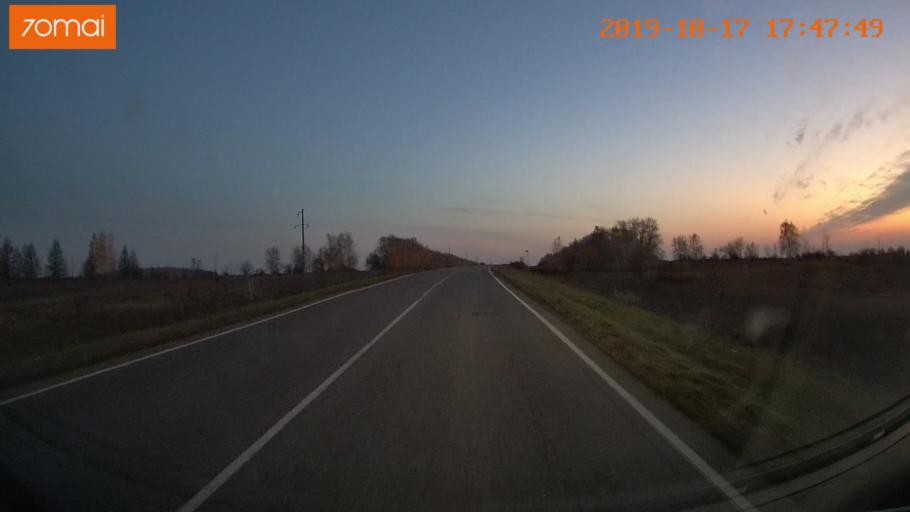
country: RU
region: Tula
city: Yepifan'
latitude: 53.7021
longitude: 38.6973
